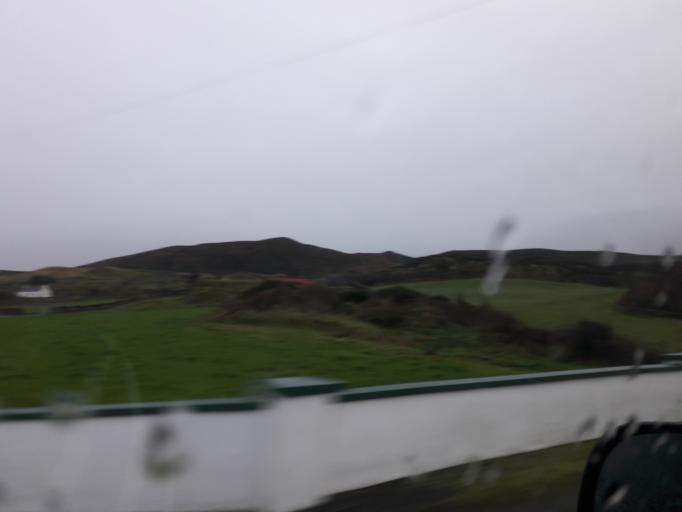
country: IE
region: Ulster
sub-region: County Donegal
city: Ramelton
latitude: 55.2671
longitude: -7.6572
